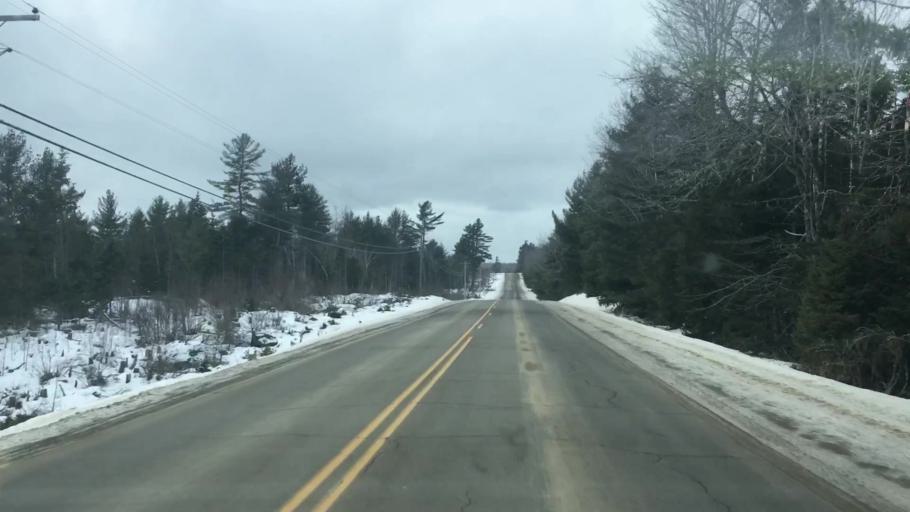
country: US
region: Maine
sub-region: Washington County
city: Calais
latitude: 45.0086
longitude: -67.4035
